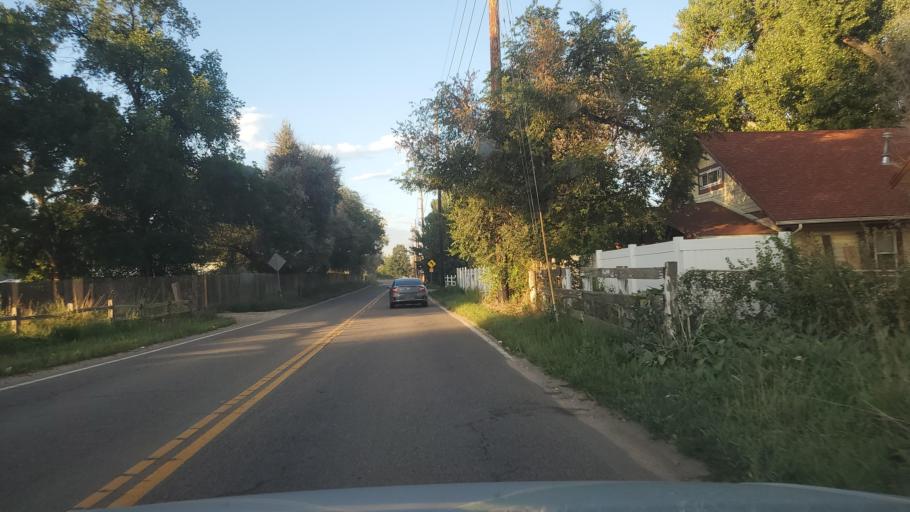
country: US
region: Colorado
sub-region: Adams County
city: Derby
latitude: 39.8674
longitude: -104.9113
